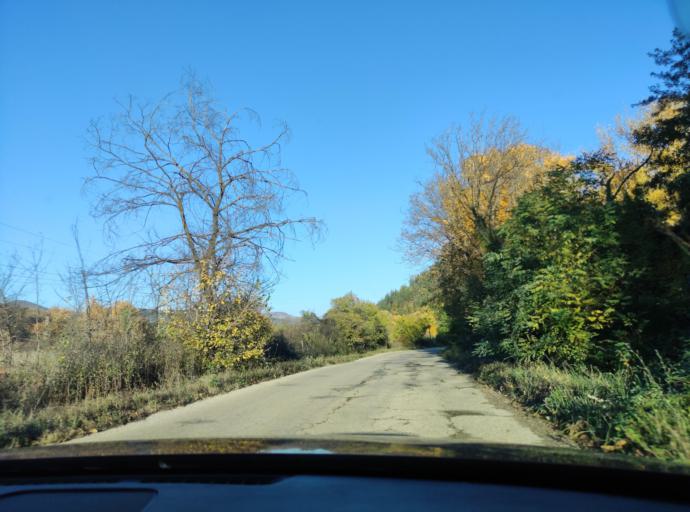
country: BG
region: Montana
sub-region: Obshtina Chiprovtsi
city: Chiprovtsi
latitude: 43.4157
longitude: 22.9473
